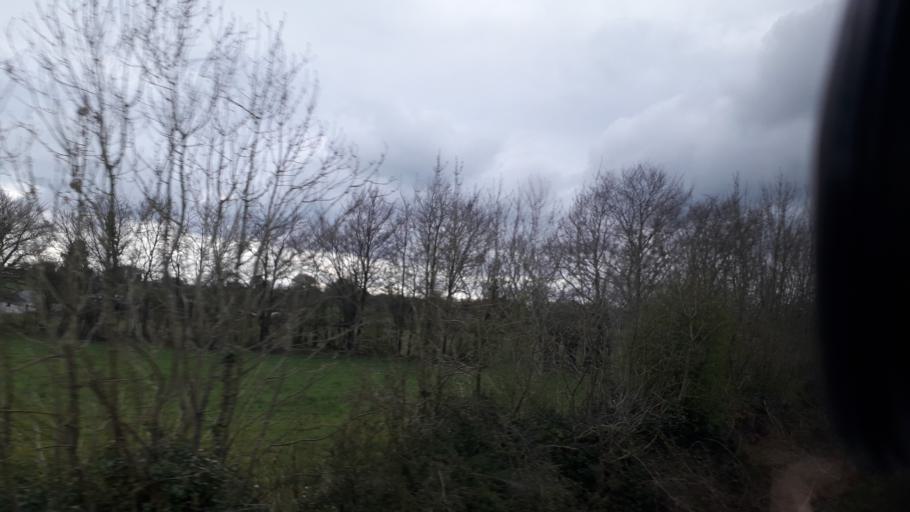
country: IE
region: Leinster
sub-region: An Longfort
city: Edgeworthstown
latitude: 53.6901
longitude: -7.6103
